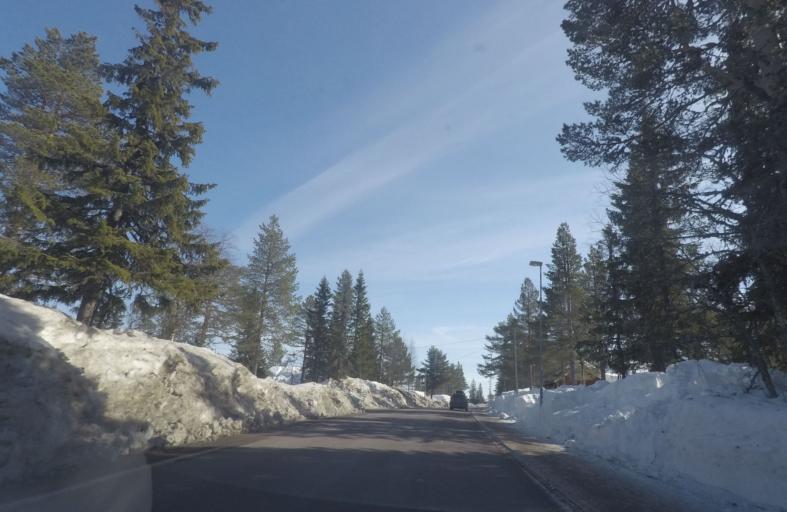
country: SE
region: Dalarna
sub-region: Malung-Saelens kommun
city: Malung
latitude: 61.1675
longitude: 13.1686
